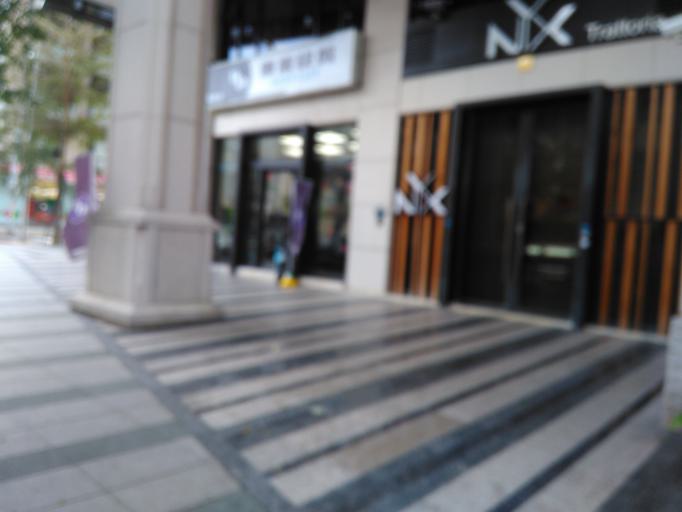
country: TW
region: Taiwan
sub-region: Hsinchu
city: Zhubei
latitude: 24.7872
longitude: 121.0208
